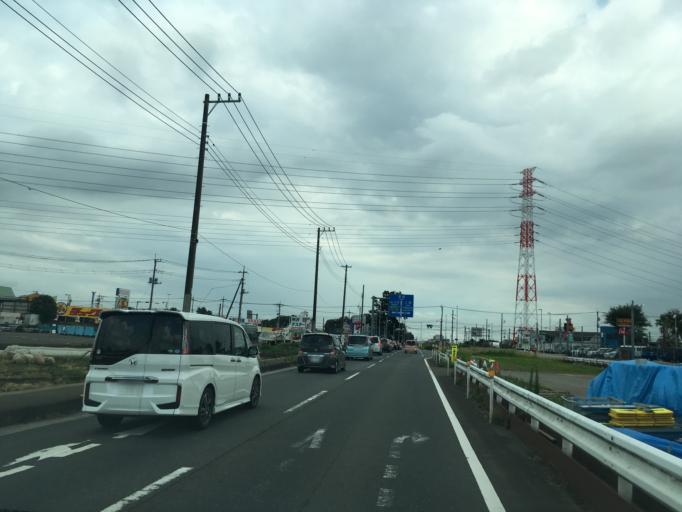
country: JP
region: Saitama
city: Tokorozawa
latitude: 35.8015
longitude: 139.4989
